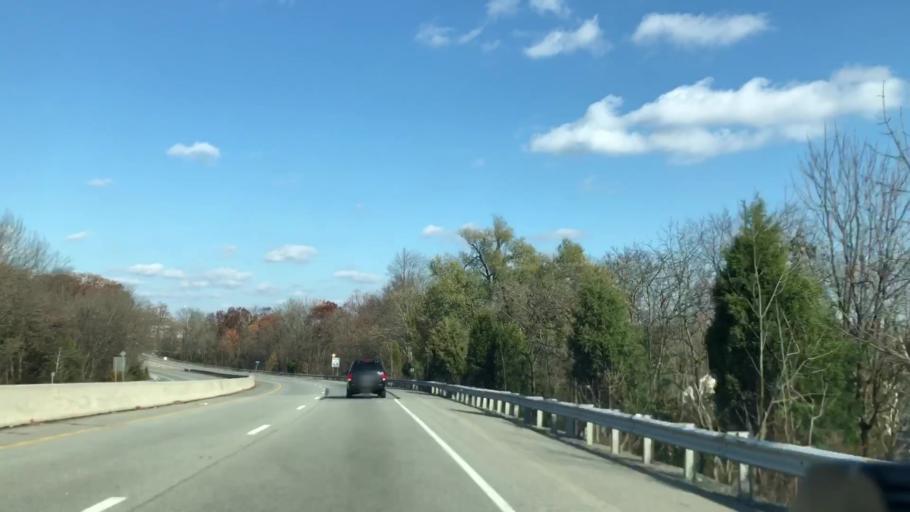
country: US
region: Pennsylvania
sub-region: Montgomery County
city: Halfway House
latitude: 40.2925
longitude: -75.6391
